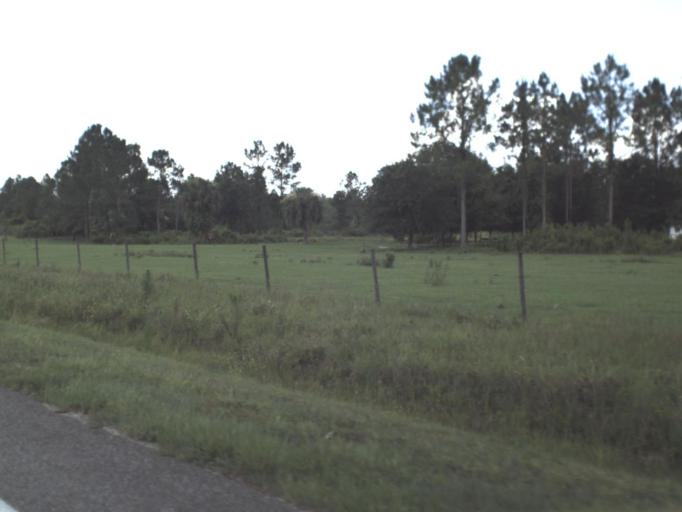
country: US
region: Florida
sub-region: Putnam County
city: East Palatka
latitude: 29.5741
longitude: -81.5525
